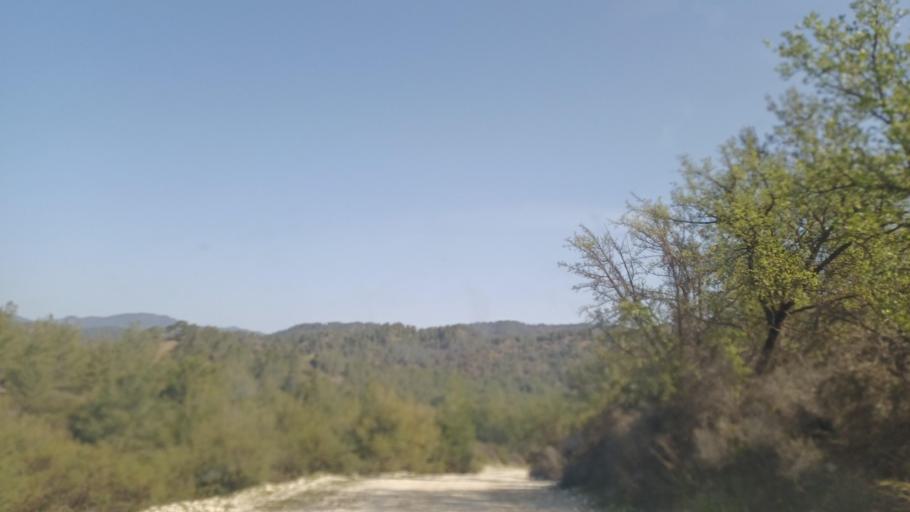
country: CY
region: Limassol
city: Pachna
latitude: 34.8897
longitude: 32.7246
